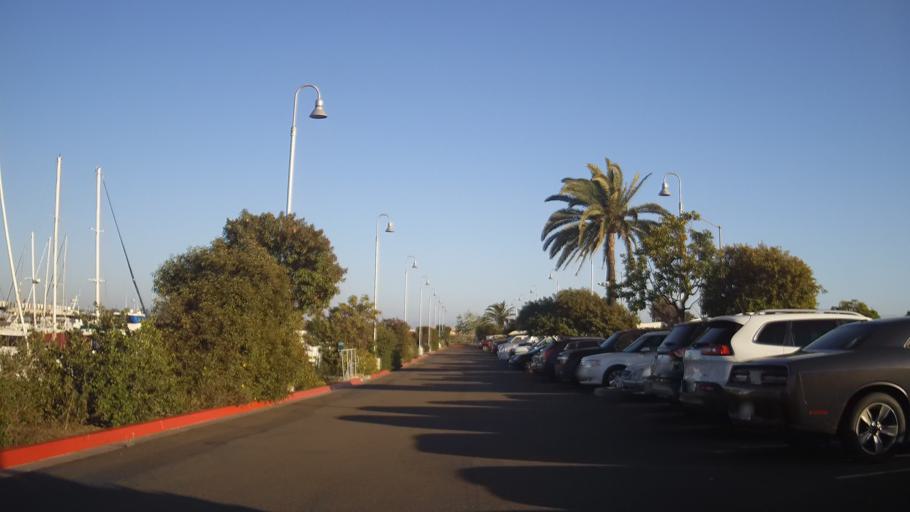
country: US
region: California
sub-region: San Diego County
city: National City
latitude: 32.6518
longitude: -117.1107
